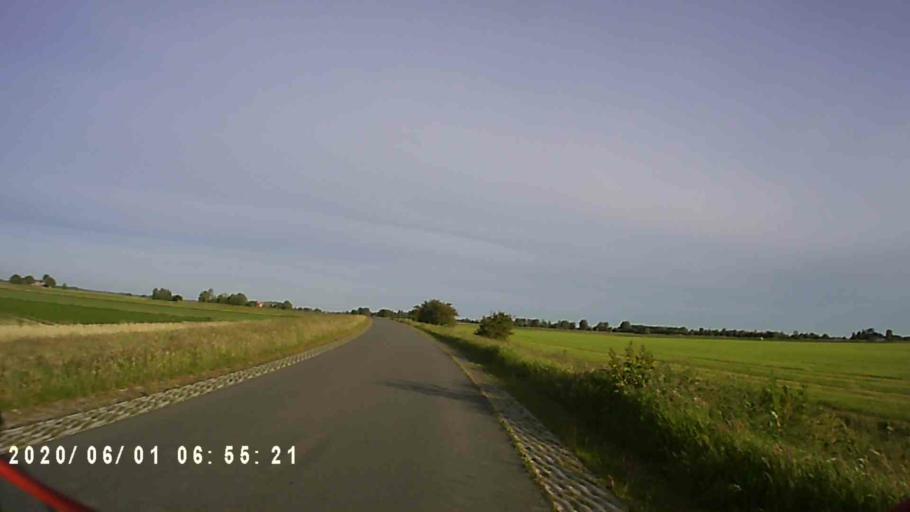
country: NL
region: Friesland
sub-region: Gemeente Kollumerland en Nieuwkruisland
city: Kollum
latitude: 53.3166
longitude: 6.1196
